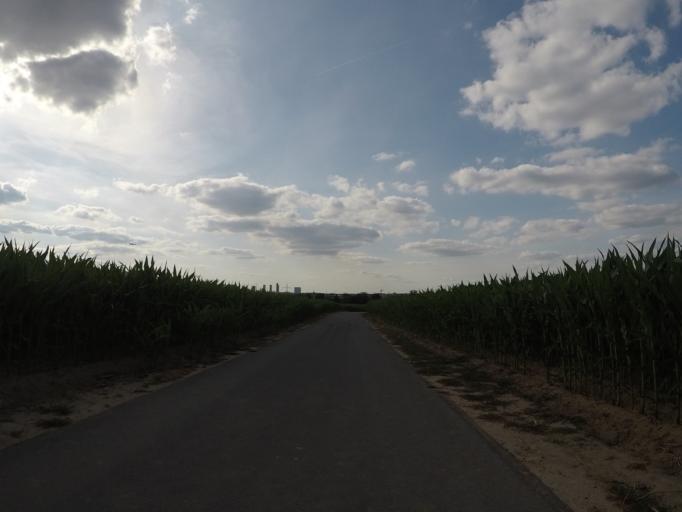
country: LU
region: Luxembourg
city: Itzig
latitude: 49.6023
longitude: 6.1795
